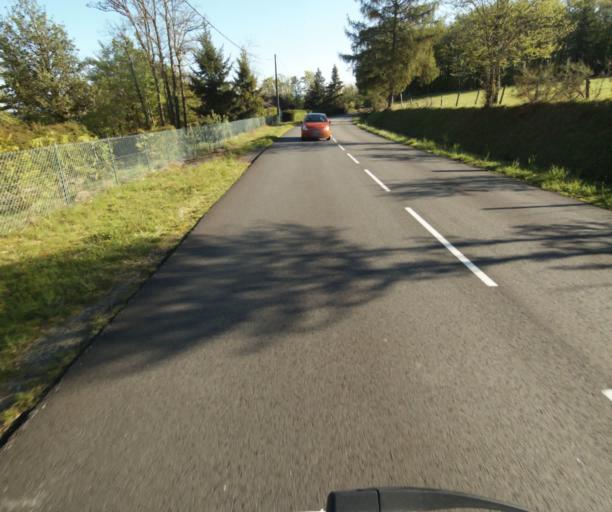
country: FR
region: Limousin
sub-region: Departement de la Correze
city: Correze
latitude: 45.3448
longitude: 1.8749
